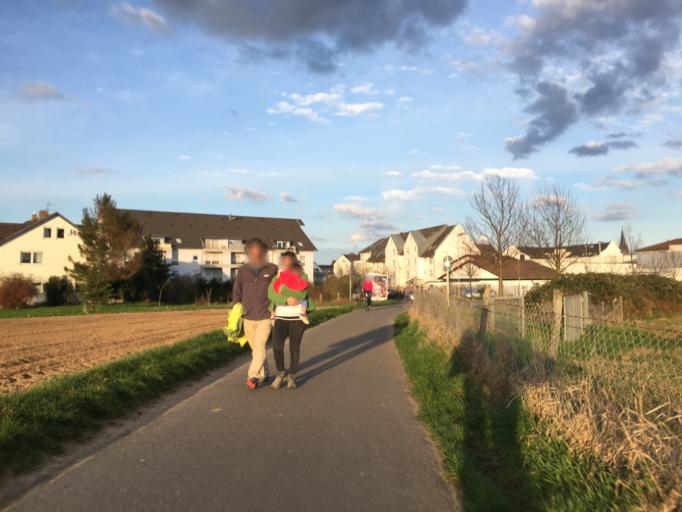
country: DE
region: North Rhine-Westphalia
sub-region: Regierungsbezirk Koln
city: Bonn
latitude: 50.7277
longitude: 7.0658
